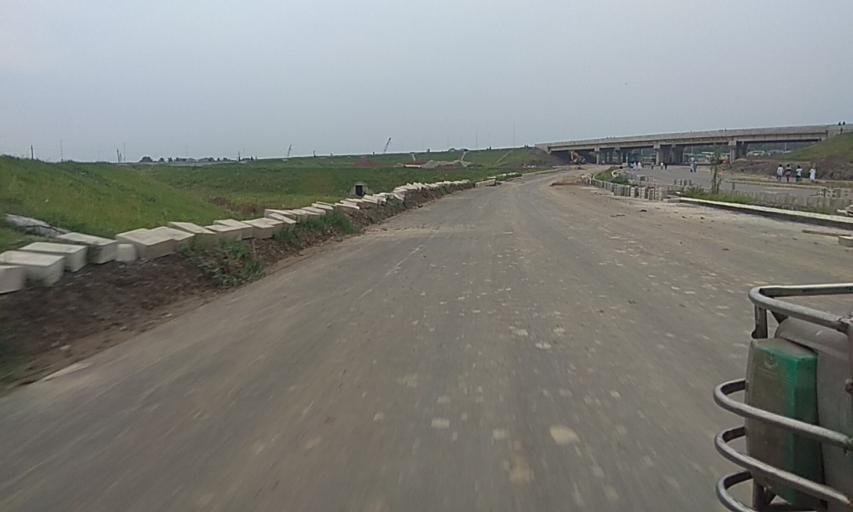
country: BD
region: Dhaka
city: Dohar
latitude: 23.3920
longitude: 89.9831
